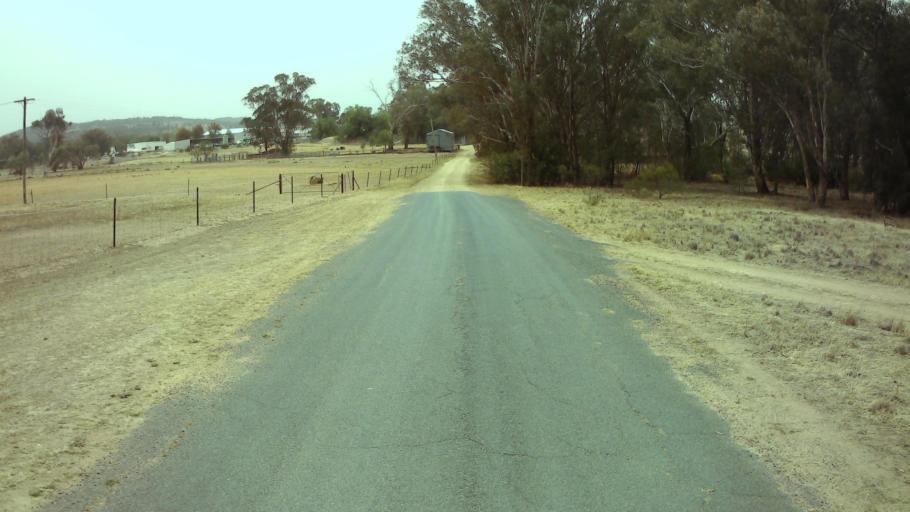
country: AU
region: New South Wales
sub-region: Weddin
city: Grenfell
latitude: -33.9055
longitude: 148.1541
